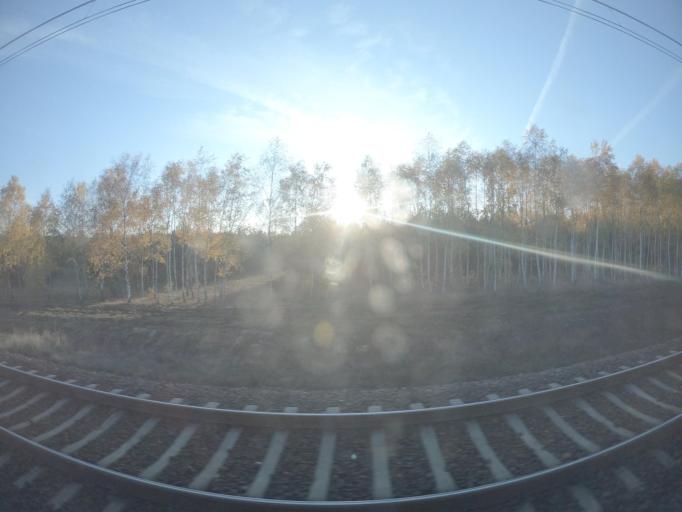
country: PL
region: Lubusz
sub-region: Powiat slubicki
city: Rzepin
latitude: 52.2877
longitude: 14.8933
